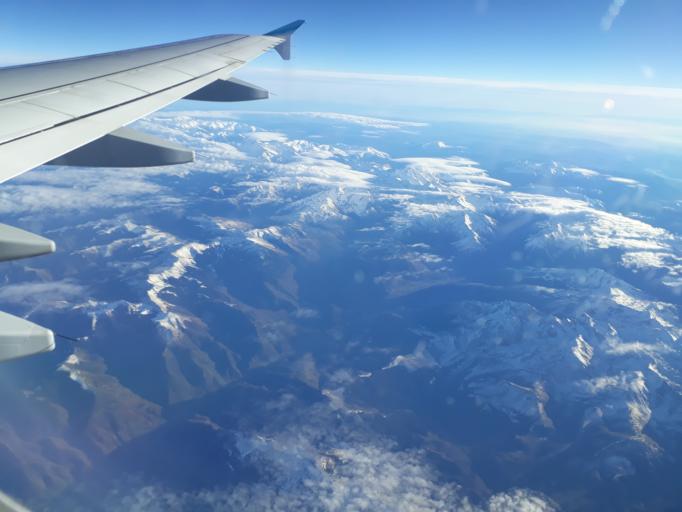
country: FR
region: Midi-Pyrenees
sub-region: Departement des Hautes-Pyrenees
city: Capvern
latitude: 43.0620
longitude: 0.2480
